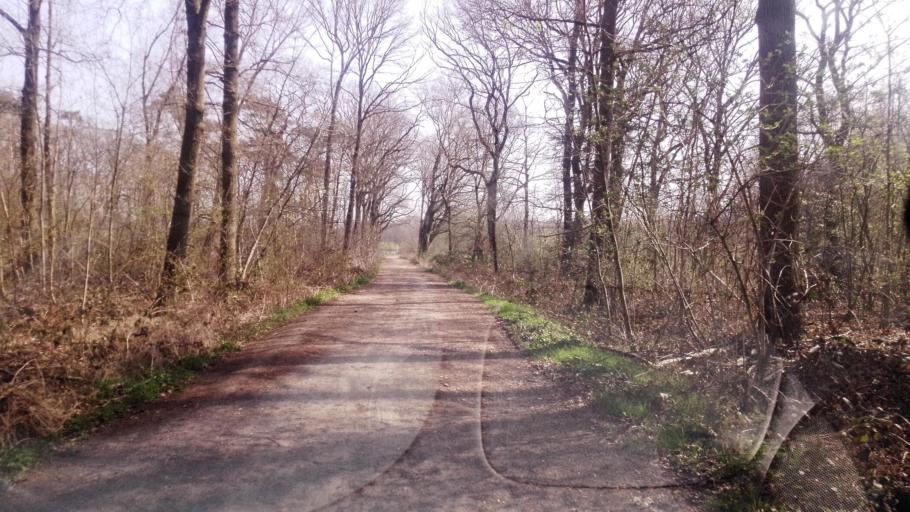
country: NL
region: Limburg
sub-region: Gemeente Peel en Maas
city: Maasbree
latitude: 51.3778
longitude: 6.0135
